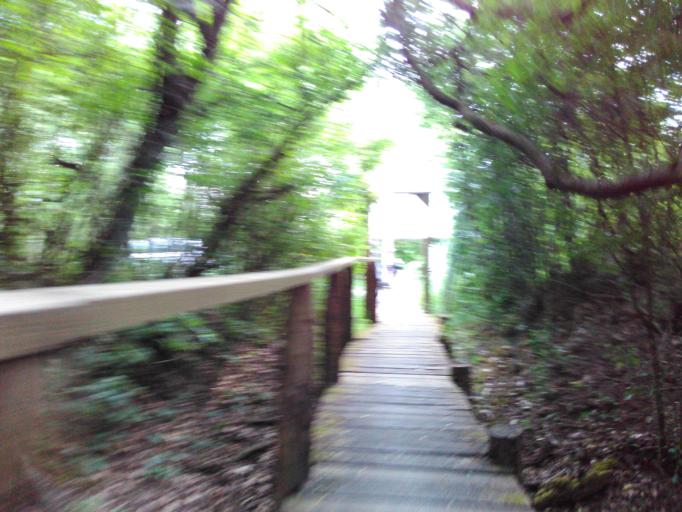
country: LU
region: Luxembourg
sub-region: Canton d'Esch-sur-Alzette
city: Schifflange
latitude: 49.5100
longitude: 6.0027
